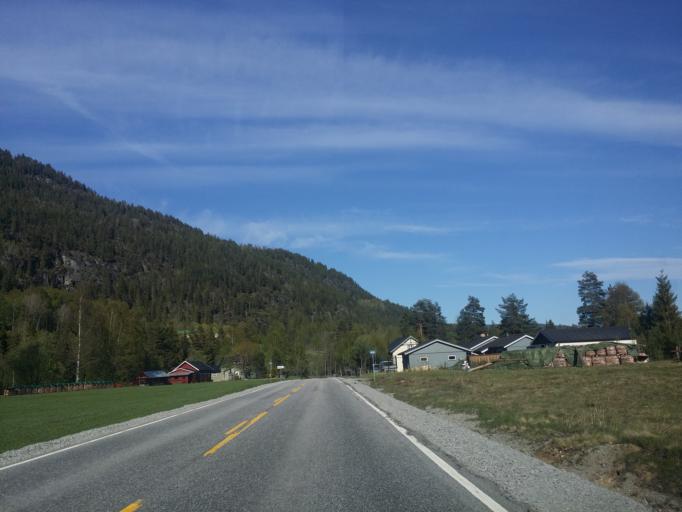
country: NO
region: Telemark
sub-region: Hjartdal
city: Sauland
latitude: 59.6230
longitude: 8.8994
